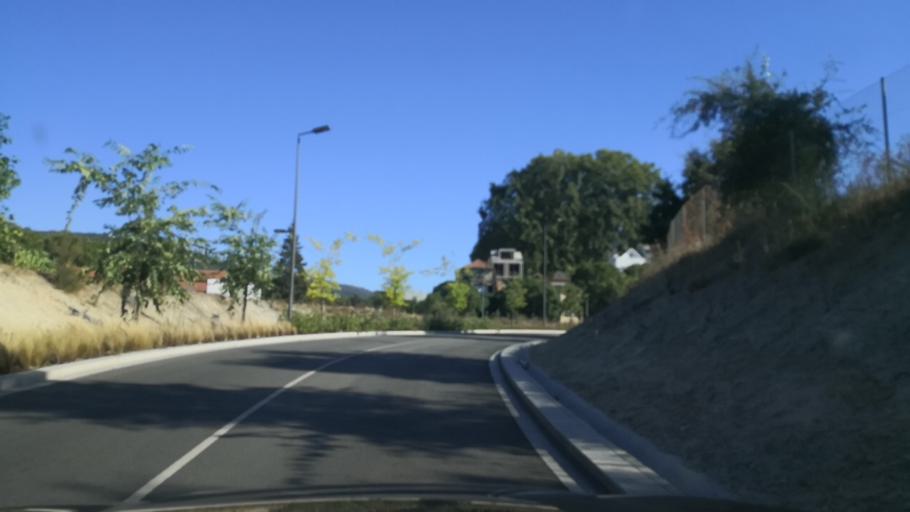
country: PT
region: Porto
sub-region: Santo Tirso
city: Santo Tirso
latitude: 41.3472
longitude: -8.4740
